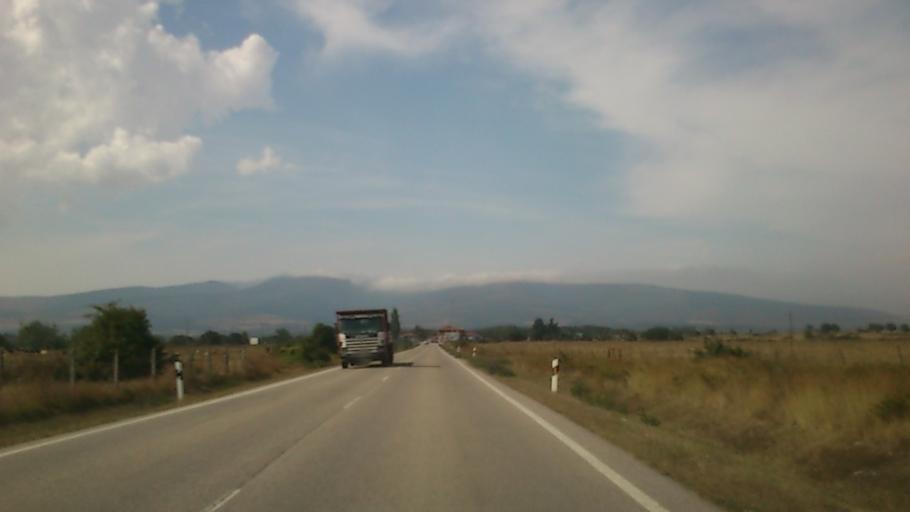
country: ES
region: Castille and Leon
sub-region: Provincia de Burgos
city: Espinosa de los Monteros
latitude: 43.0435
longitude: -3.4847
